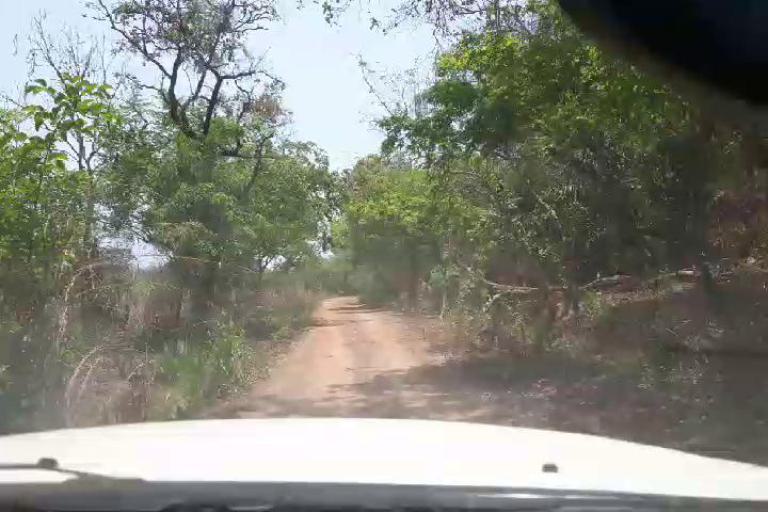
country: SL
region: Northern Province
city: Alikalia
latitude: 9.0808
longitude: -11.4684
